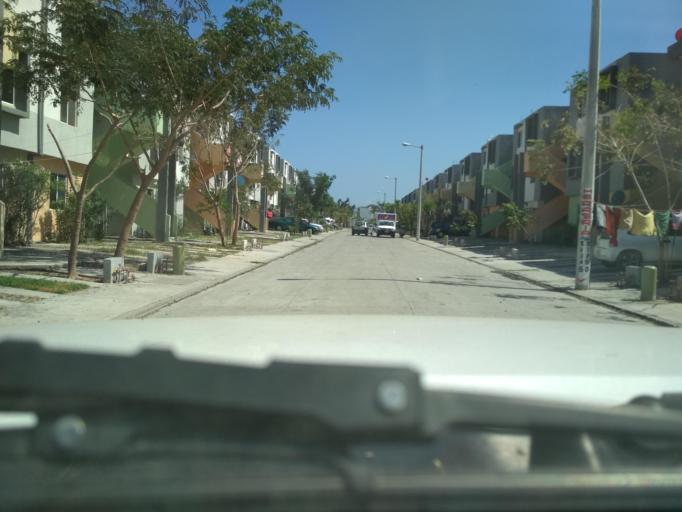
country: MX
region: Veracruz
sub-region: Medellin
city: Fraccionamiento Arboledas San Ramon
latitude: 19.0904
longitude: -96.1667
